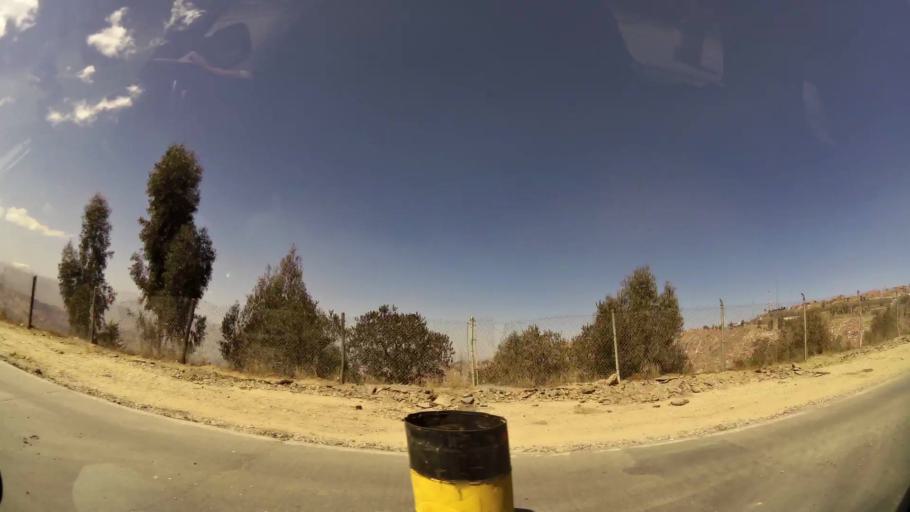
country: BO
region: La Paz
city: La Paz
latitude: -16.4861
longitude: -68.1603
